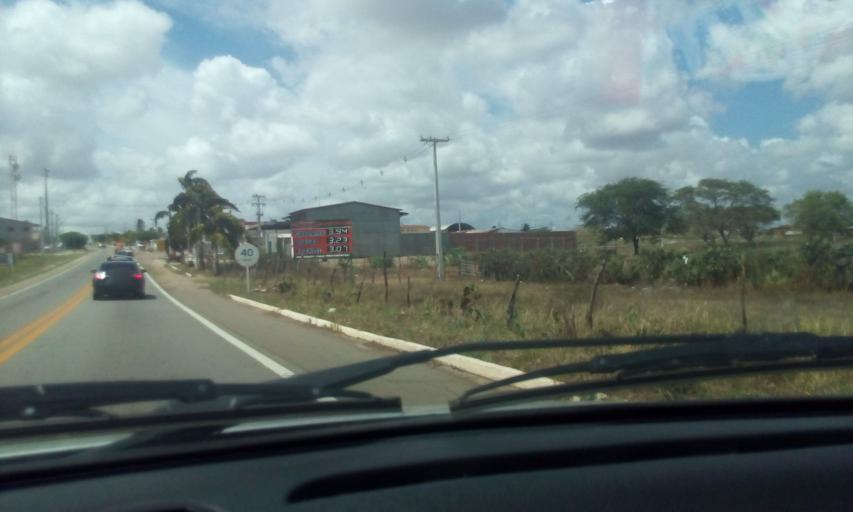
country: BR
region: Rio Grande do Norte
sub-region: Sao Paulo Do Potengi
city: Sao Paulo do Potengi
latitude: -5.9808
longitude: -35.5791
